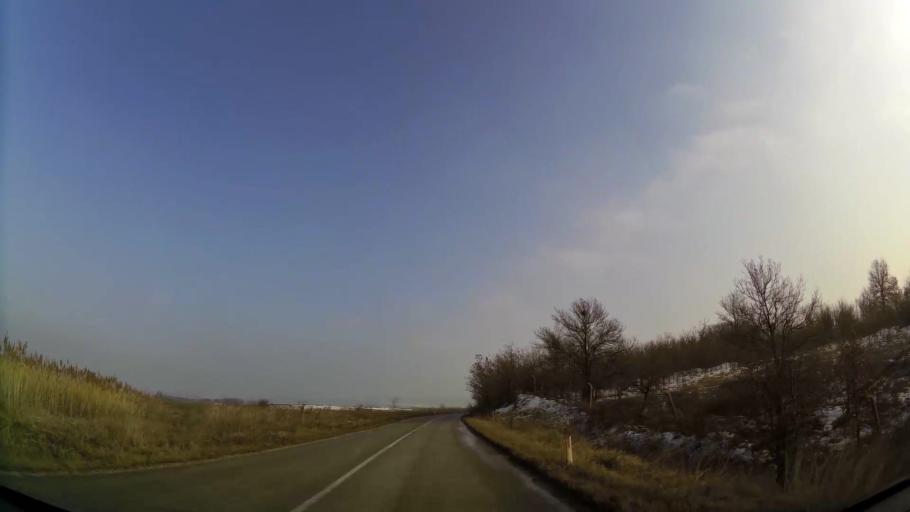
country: MK
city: Miladinovci
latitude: 41.9769
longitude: 21.6288
